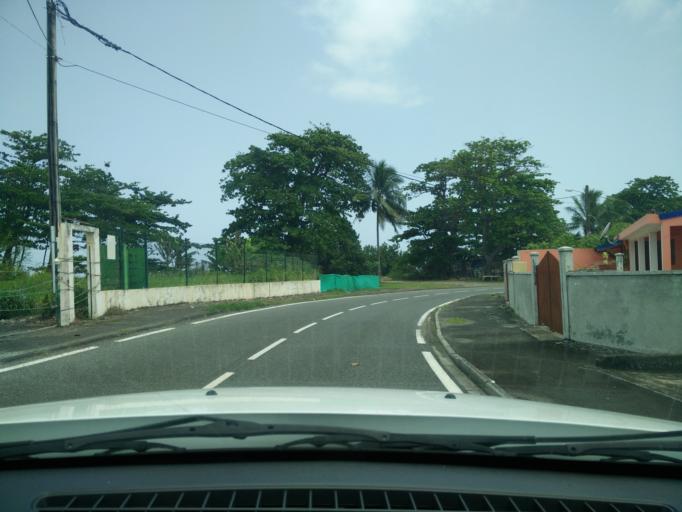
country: GP
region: Guadeloupe
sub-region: Guadeloupe
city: Capesterre-Belle-Eau
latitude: 16.0509
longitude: -61.5578
